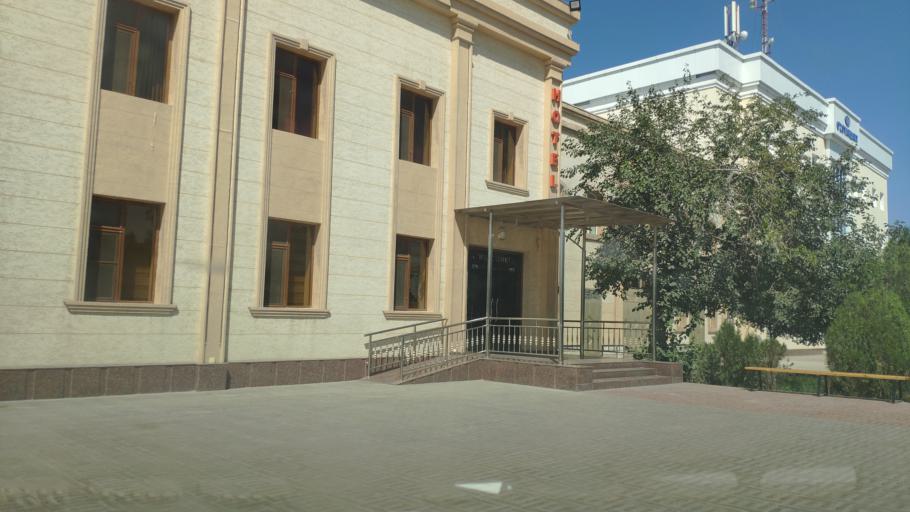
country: UZ
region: Xorazm
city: Urganch
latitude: 41.5343
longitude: 60.6613
